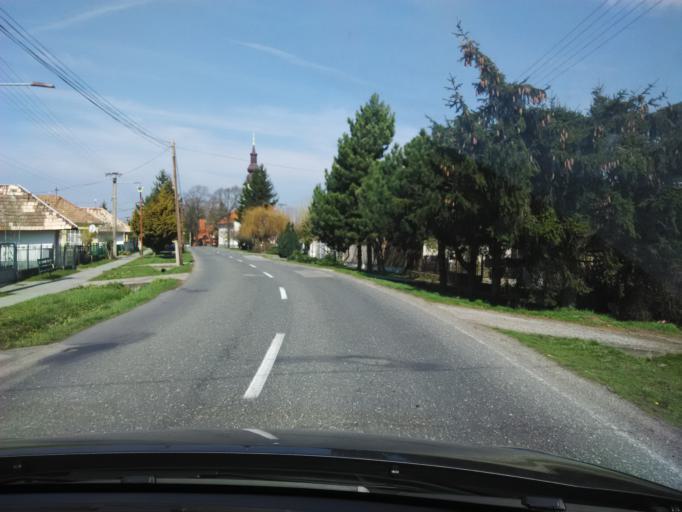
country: SK
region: Nitriansky
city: Tlmace
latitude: 48.2416
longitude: 18.5209
